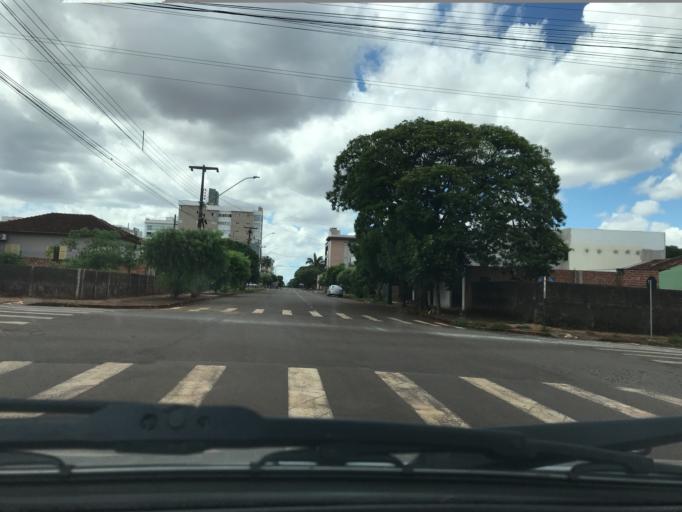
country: BR
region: Parana
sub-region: Palotina
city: Palotina
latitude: -24.2883
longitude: -53.8371
